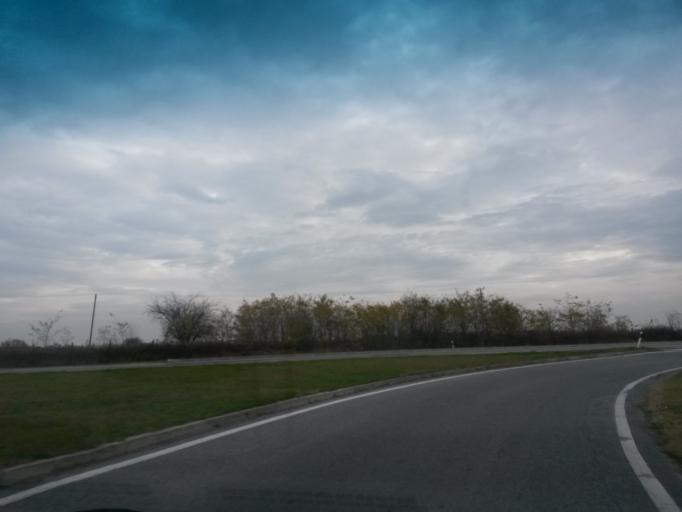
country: HR
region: Osjecko-Baranjska
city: Tenja
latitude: 45.5237
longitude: 18.7772
